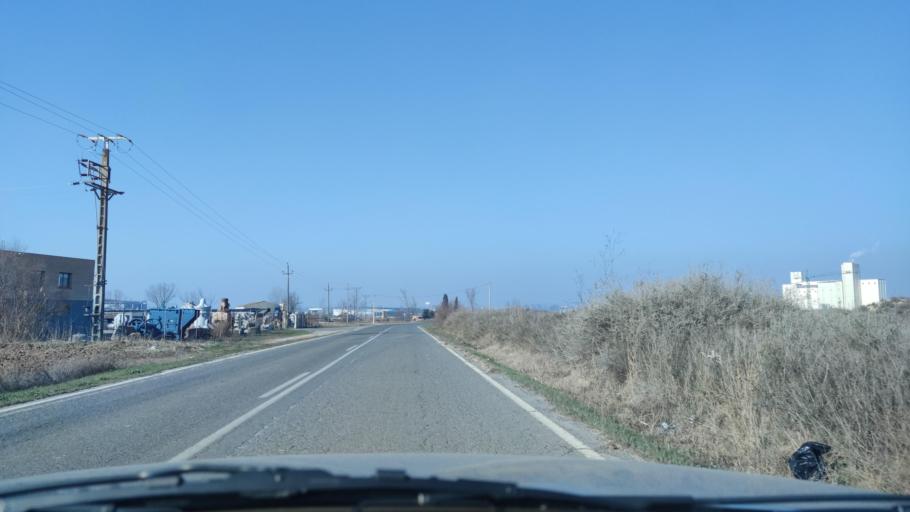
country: ES
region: Catalonia
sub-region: Provincia de Lleida
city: Alcoletge
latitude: 41.6227
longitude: 0.7253
